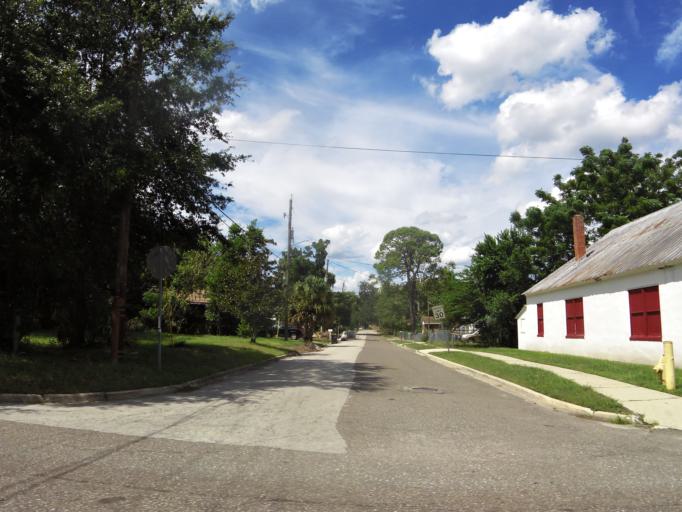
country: US
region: Florida
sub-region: Duval County
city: Jacksonville
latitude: 30.3849
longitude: -81.6448
